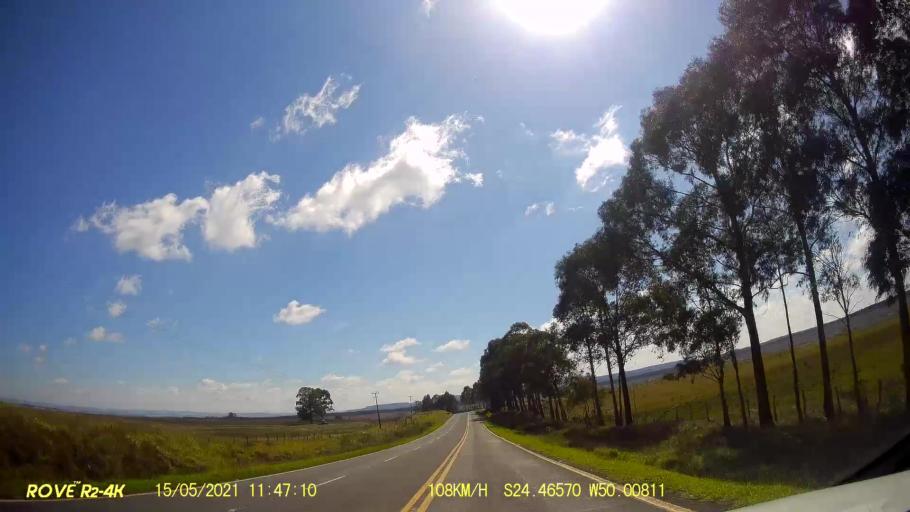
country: BR
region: Parana
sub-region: Pirai Do Sul
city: Pirai do Sul
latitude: -24.4658
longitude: -50.0081
